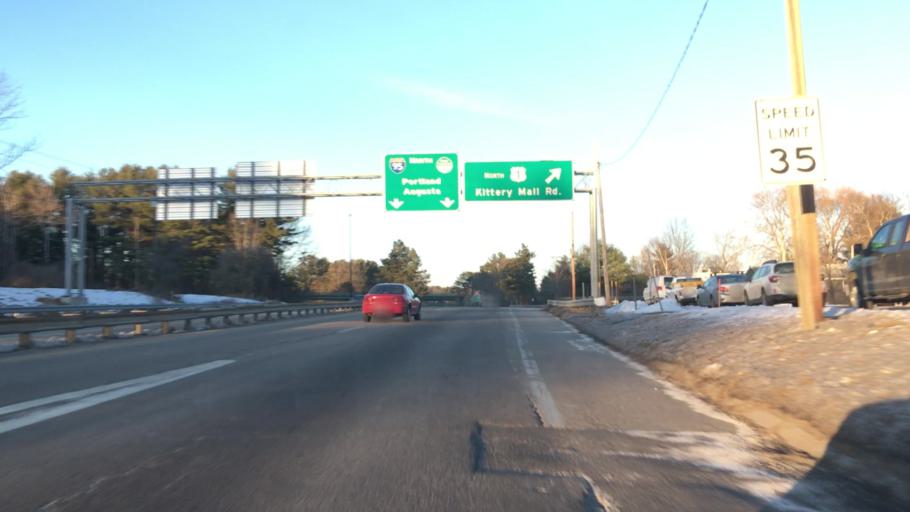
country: US
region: Maine
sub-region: York County
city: Kittery
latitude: 43.1042
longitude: -70.7430
